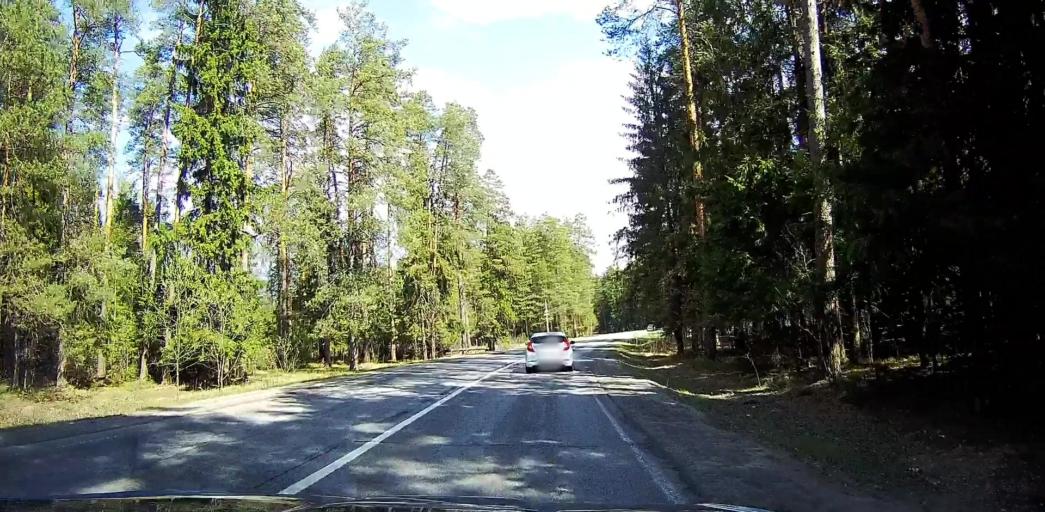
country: RU
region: Moskovskaya
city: Davydovo
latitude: 55.5659
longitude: 38.8618
